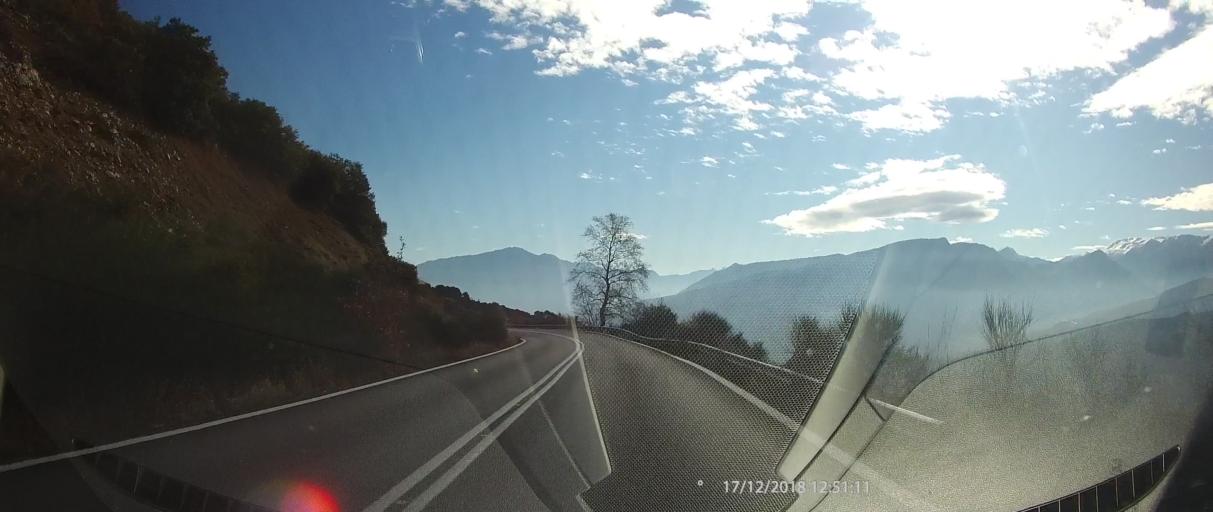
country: GR
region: Thessaly
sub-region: Trikala
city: Kastraki
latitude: 39.7694
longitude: 21.4616
